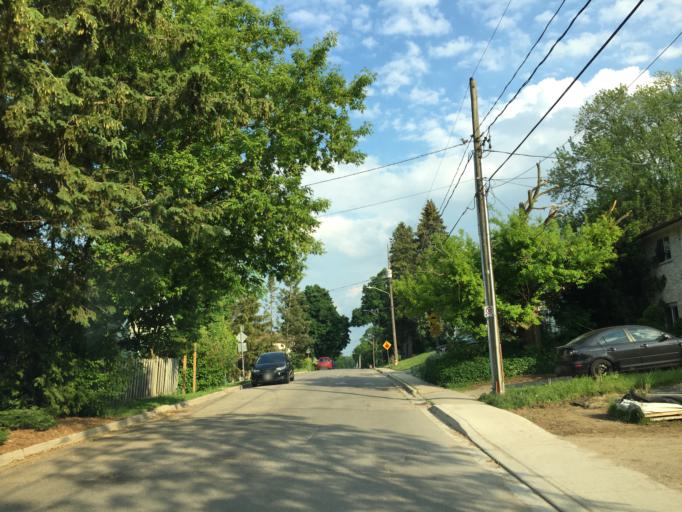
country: CA
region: Ontario
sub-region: Wellington County
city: Guelph
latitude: 43.5528
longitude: -80.2688
